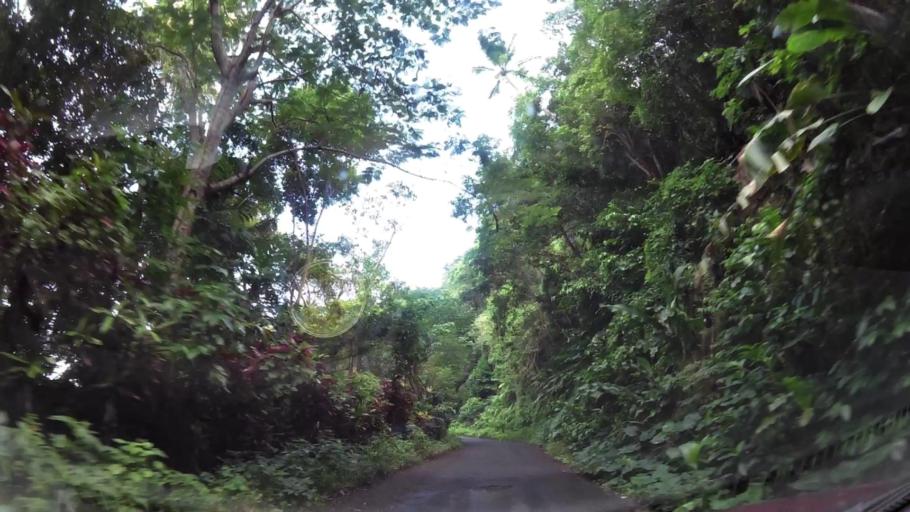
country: DM
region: Saint Andrew
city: Marigot
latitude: 15.5155
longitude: -61.2734
